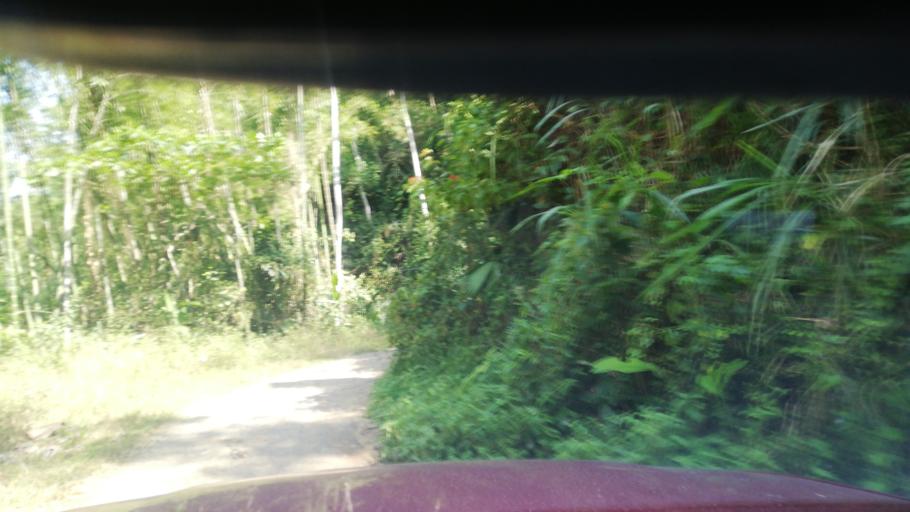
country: CO
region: Risaralda
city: Balboa
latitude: 4.9041
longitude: -75.9419
